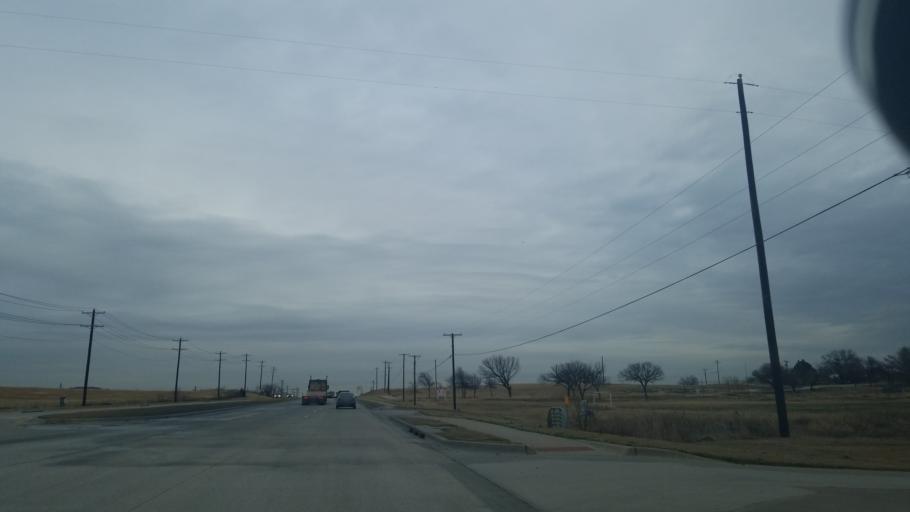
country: US
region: Texas
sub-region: Denton County
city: Denton
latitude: 33.2302
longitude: -97.1845
